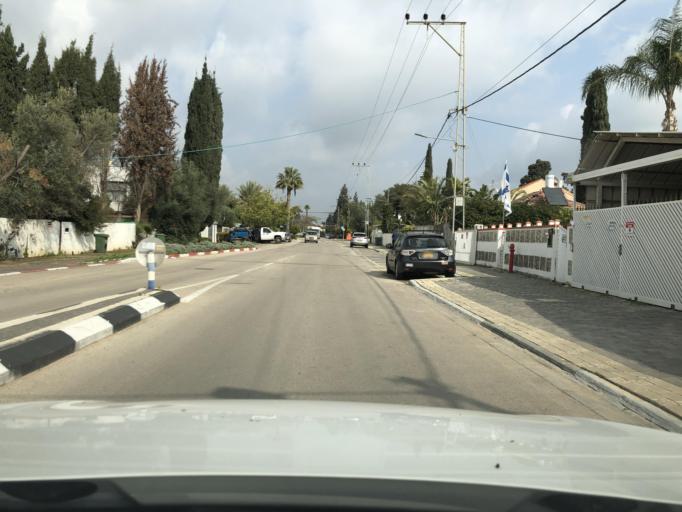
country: IL
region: Central District
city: Yehud
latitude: 32.0346
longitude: 34.8979
